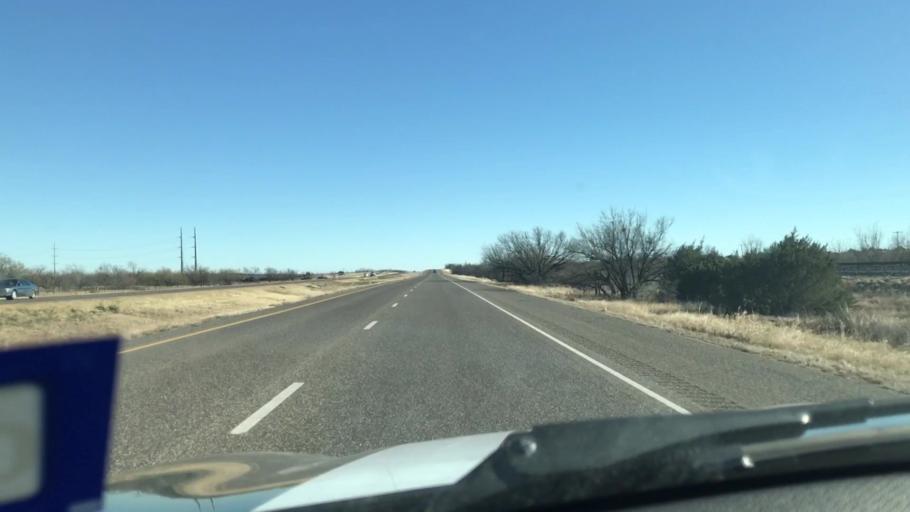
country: US
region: Texas
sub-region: Scurry County
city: Snyder
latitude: 32.8445
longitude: -101.0026
